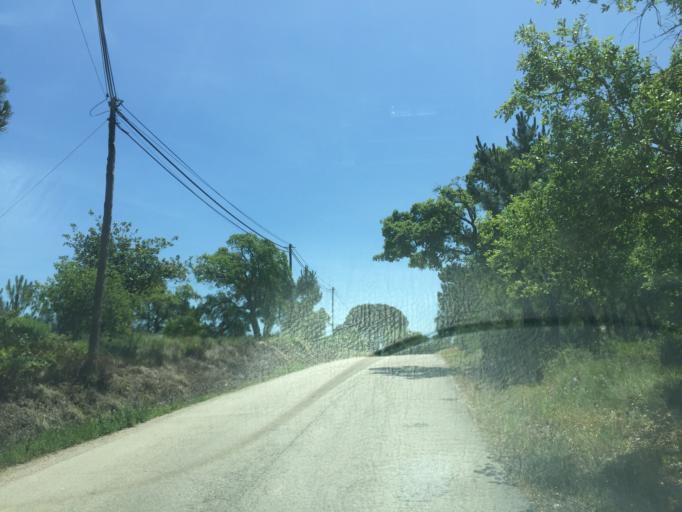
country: PT
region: Lisbon
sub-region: Mafra
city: Venda do Pinheiro
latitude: 38.8920
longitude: -9.2276
